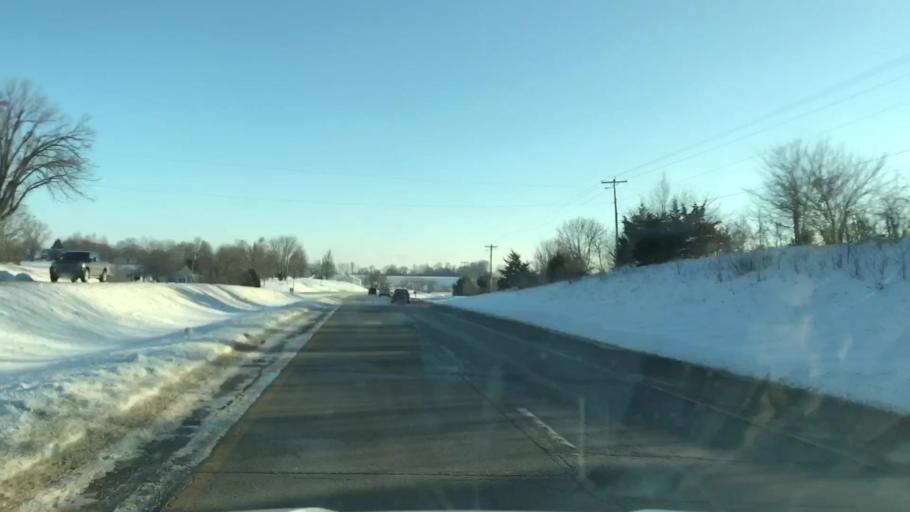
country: US
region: Missouri
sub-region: Andrew County
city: Country Club Village
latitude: 39.8698
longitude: -94.8086
